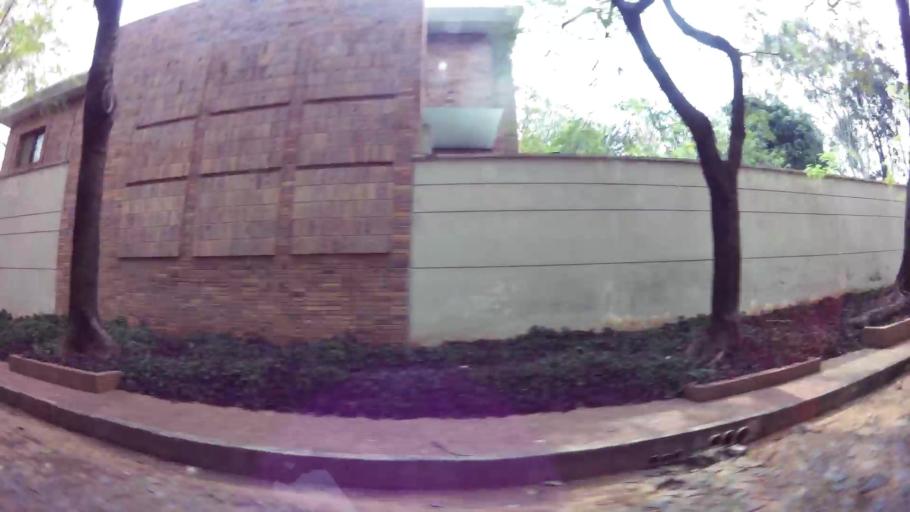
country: PY
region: Central
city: Fernando de la Mora
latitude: -25.2769
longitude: -57.5595
